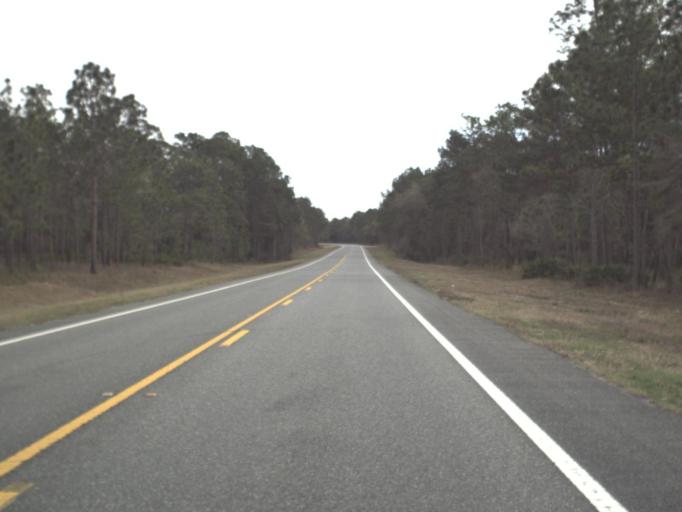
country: US
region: Florida
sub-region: Wakulla County
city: Crawfordville
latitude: 30.2956
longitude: -84.4114
